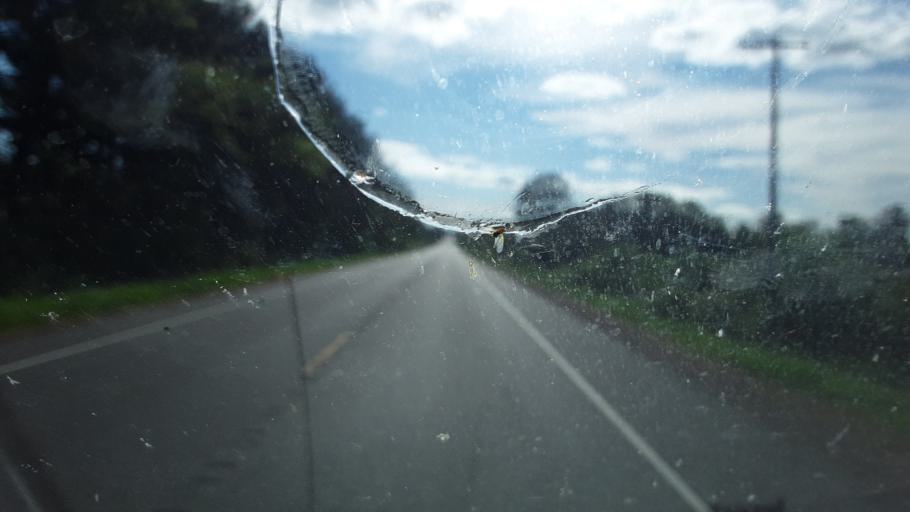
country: US
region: Wisconsin
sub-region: Wood County
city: Marshfield
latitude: 44.6558
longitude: -90.2147
